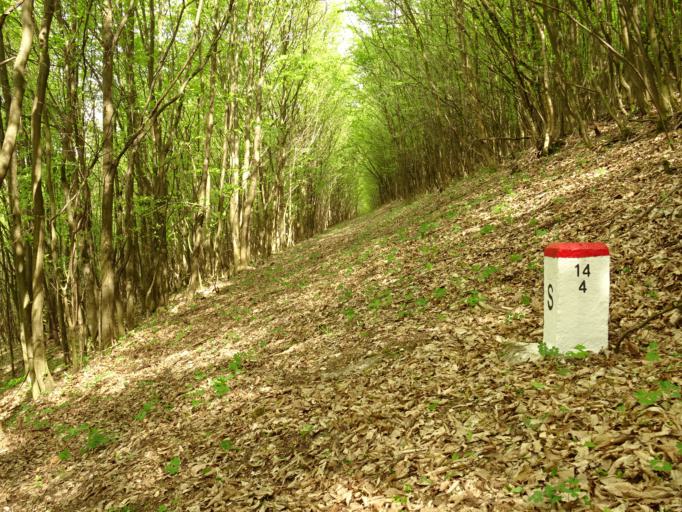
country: SK
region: Kosicky
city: Moldava nad Bodvou
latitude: 48.5565
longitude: 20.9014
